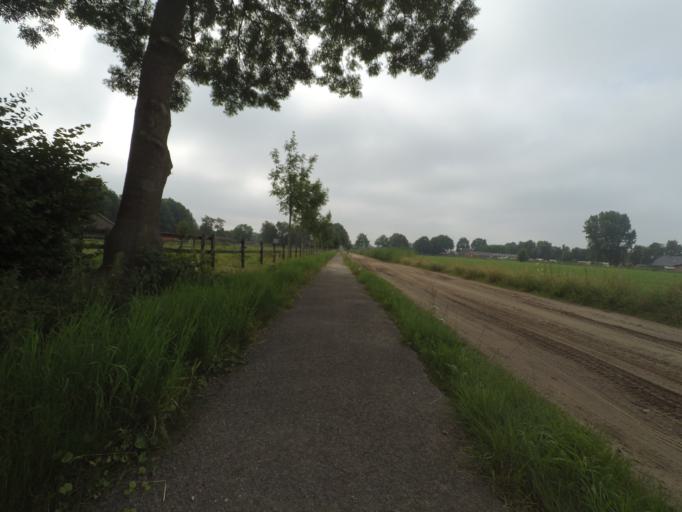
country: NL
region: Gelderland
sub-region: Gemeente Barneveld
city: Kootwijkerbroek
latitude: 52.1232
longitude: 5.6565
